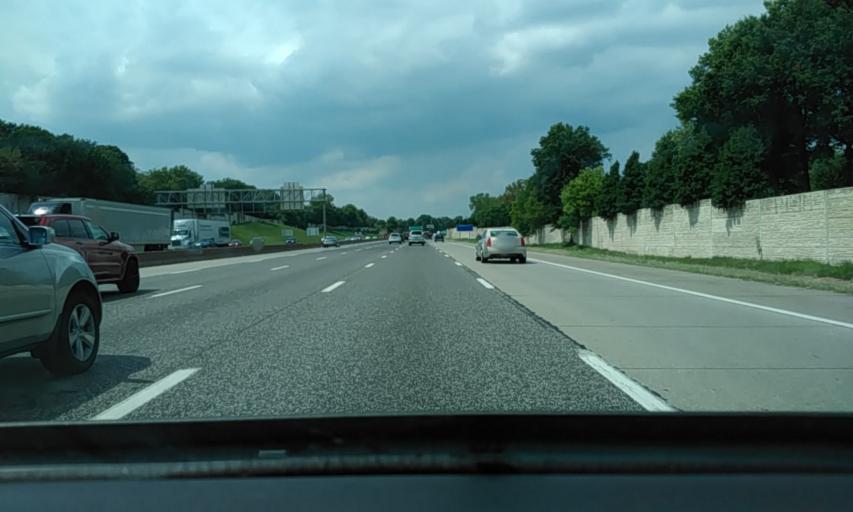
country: US
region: Missouri
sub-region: Saint Louis County
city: Sappington
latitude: 38.5160
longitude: -90.3817
